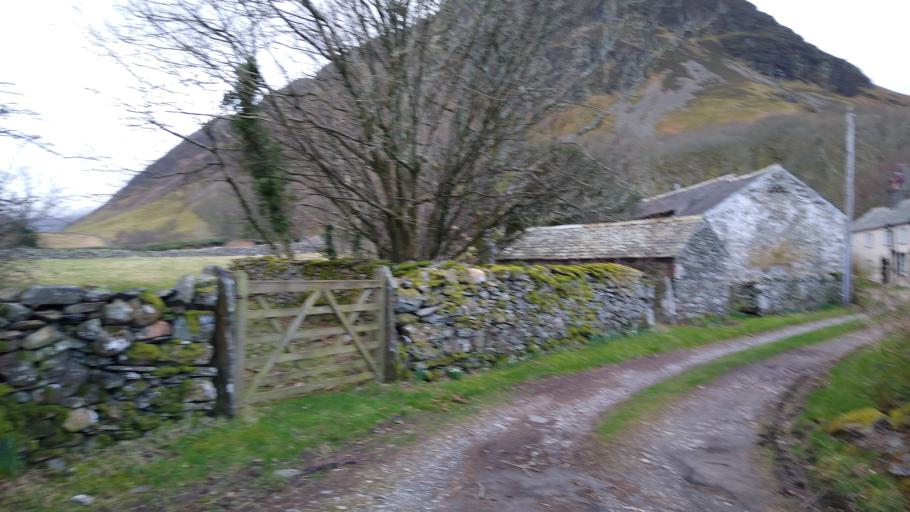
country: GB
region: England
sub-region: Cumbria
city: Cockermouth
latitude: 54.5721
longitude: -3.3244
